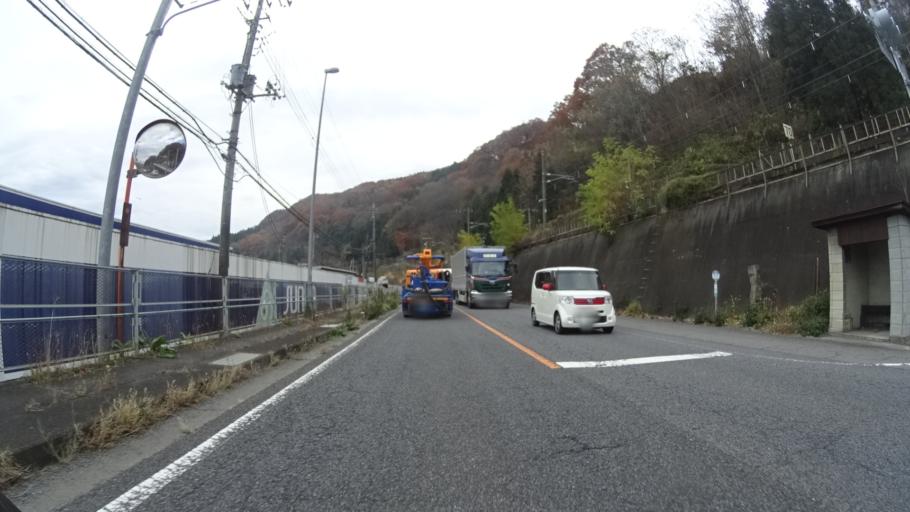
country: JP
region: Gunma
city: Numata
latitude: 36.6122
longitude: 139.0416
